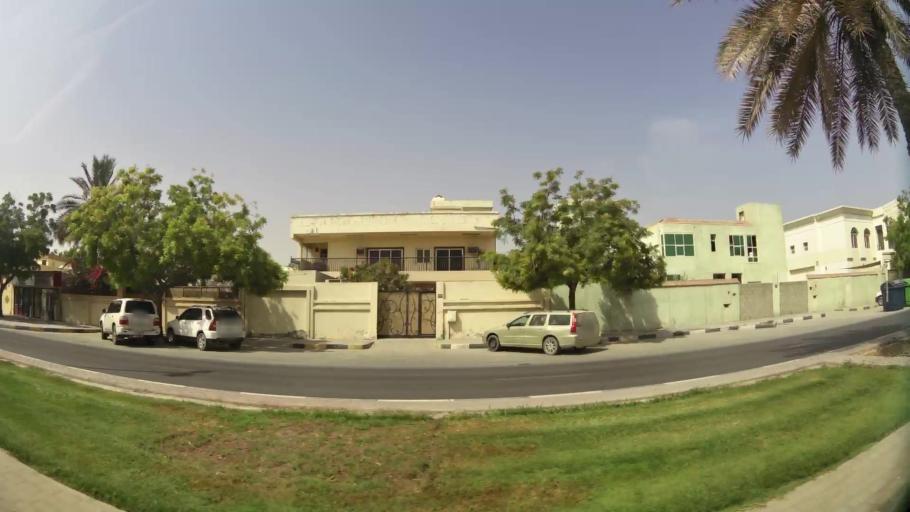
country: AE
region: Ash Shariqah
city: Sharjah
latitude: 25.3715
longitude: 55.4109
